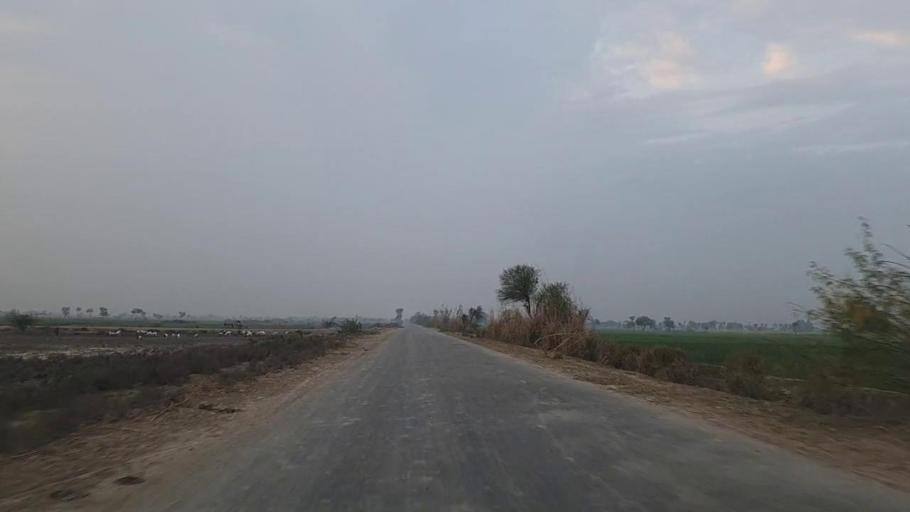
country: PK
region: Sindh
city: Jam Sahib
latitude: 26.3188
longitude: 68.5620
